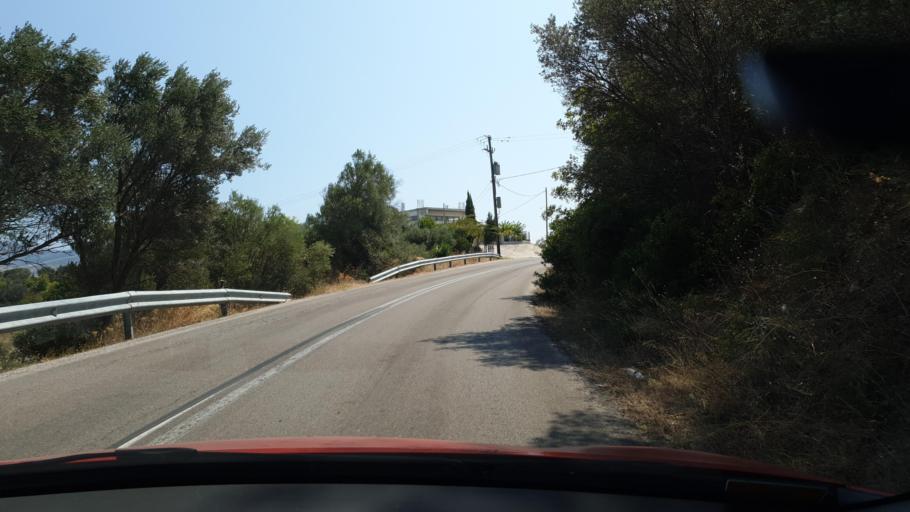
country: GR
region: Central Greece
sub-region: Nomos Evvoias
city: Oxilithos
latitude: 38.5334
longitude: 24.0835
